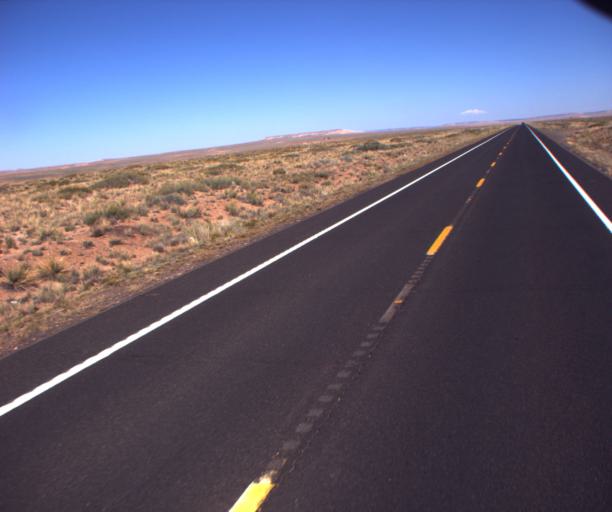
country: US
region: Arizona
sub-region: Coconino County
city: Tuba City
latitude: 36.1567
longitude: -111.1170
